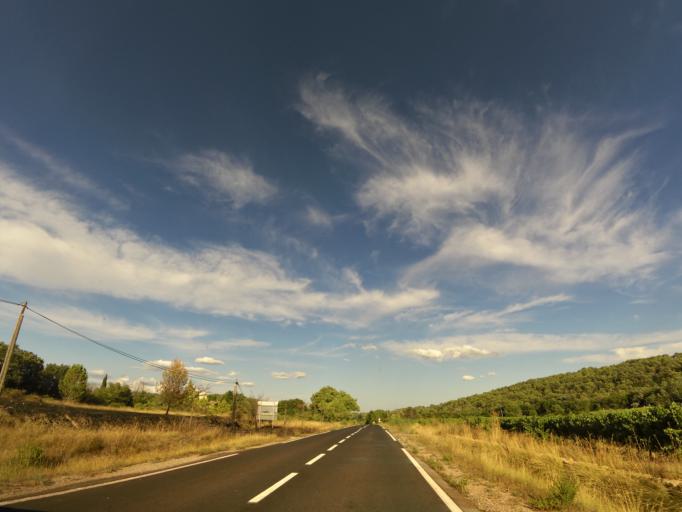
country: FR
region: Languedoc-Roussillon
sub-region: Departement de l'Herault
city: Saint-Drezery
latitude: 43.7678
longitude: 3.9747
